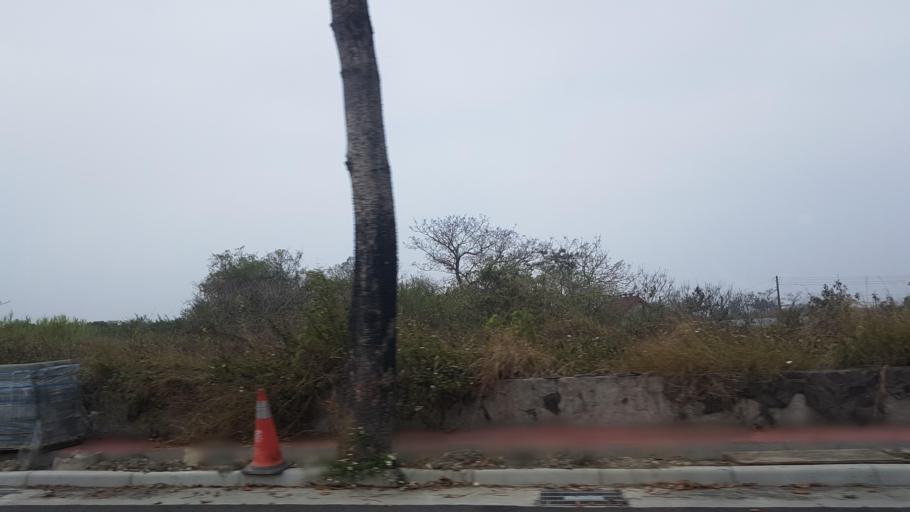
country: TW
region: Taiwan
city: Xinying
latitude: 23.3177
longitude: 120.3047
